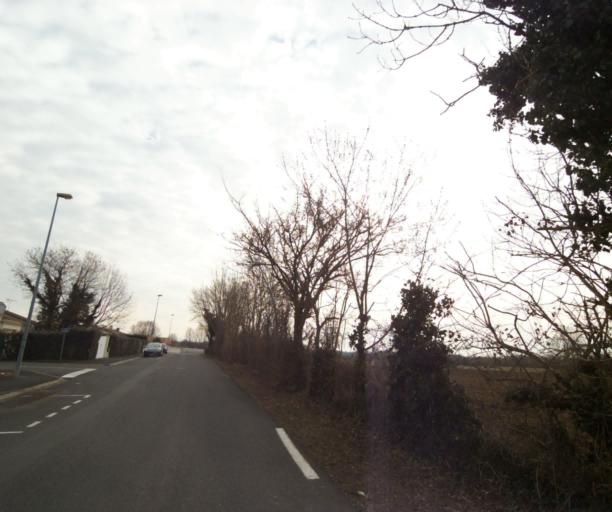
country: FR
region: Poitou-Charentes
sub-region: Departement des Deux-Sevres
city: Niort
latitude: 46.3072
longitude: -0.4540
